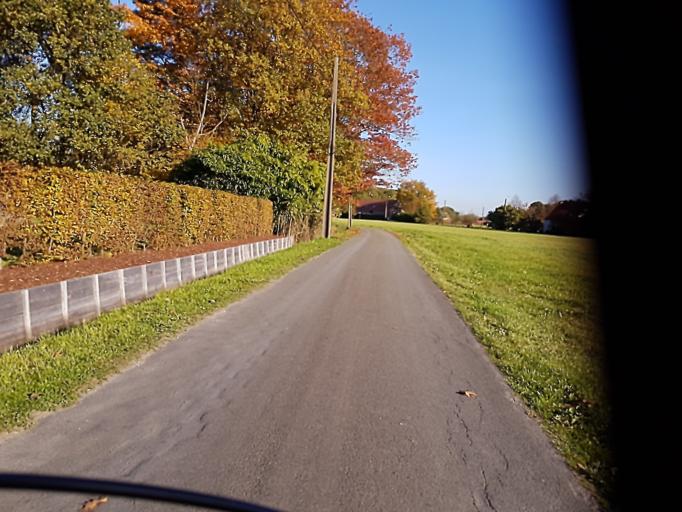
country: BE
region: Flanders
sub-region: Provincie Antwerpen
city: Bonheiden
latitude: 51.0431
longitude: 4.5673
